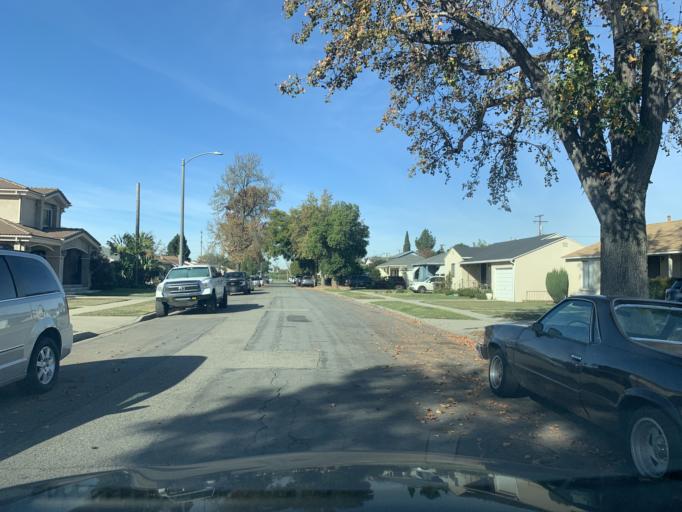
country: US
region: California
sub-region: Los Angeles County
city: East Rancho Dominguez
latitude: 33.8622
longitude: -118.1924
